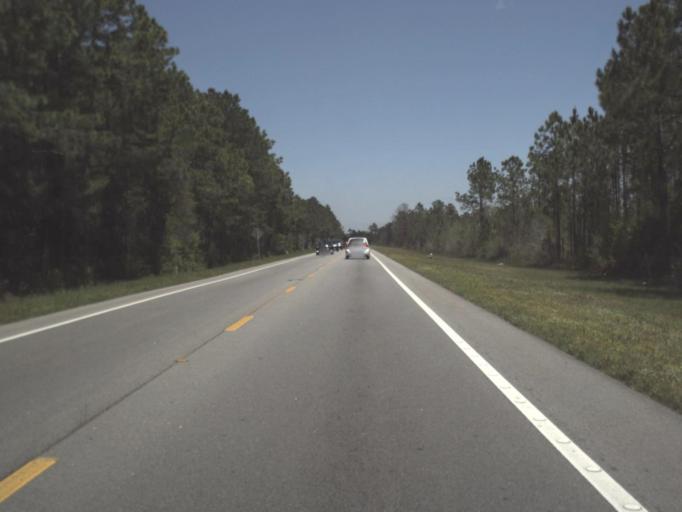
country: US
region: Florida
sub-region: Escambia County
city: Myrtle Grove
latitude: 30.3852
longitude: -87.3481
